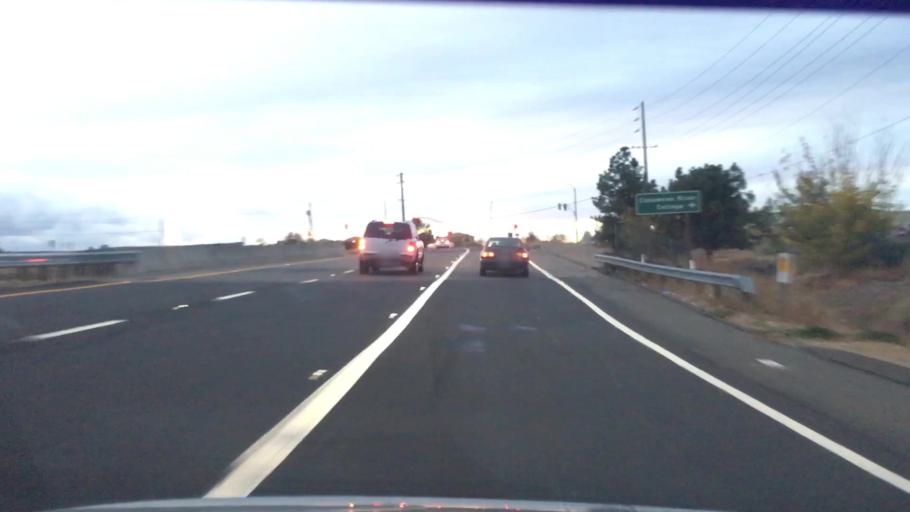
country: US
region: California
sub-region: Sacramento County
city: Florin
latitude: 38.4585
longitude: -121.4126
